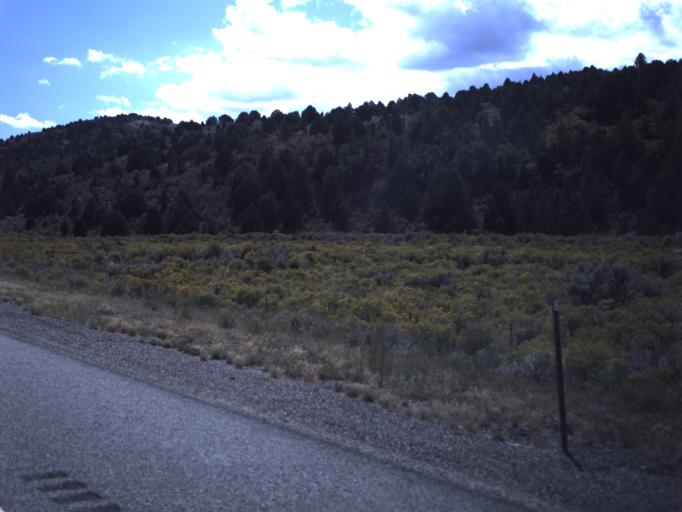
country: US
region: Utah
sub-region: Sevier County
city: Salina
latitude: 38.8010
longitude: -111.5161
